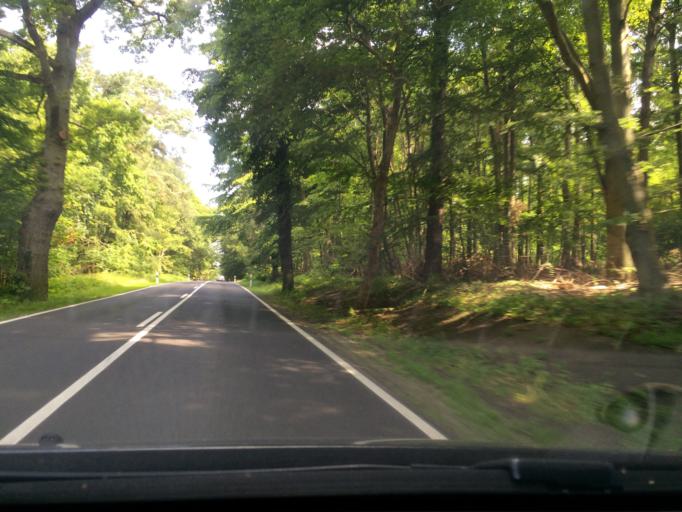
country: DE
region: Mecklenburg-Vorpommern
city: Ostseebad Binz
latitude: 54.4297
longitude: 13.5512
